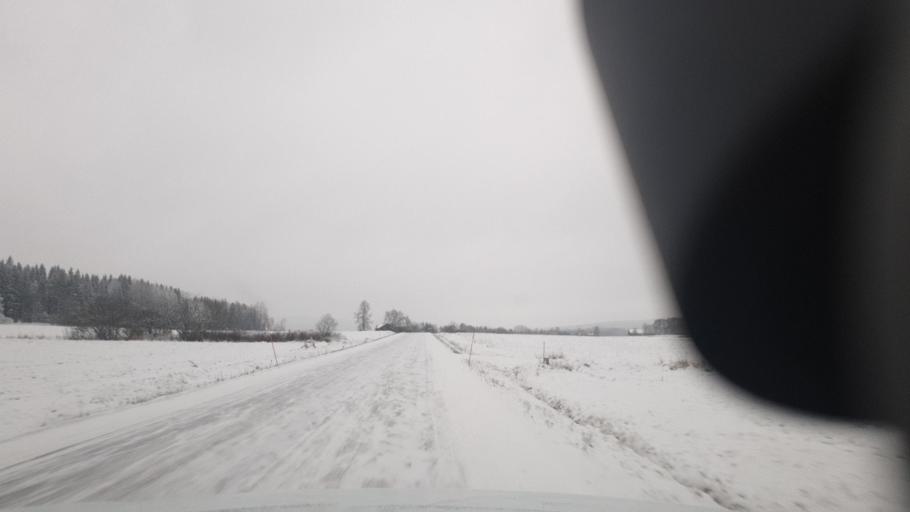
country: SE
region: Vaermland
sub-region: Eda Kommun
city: Charlottenberg
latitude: 59.7564
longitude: 12.1576
